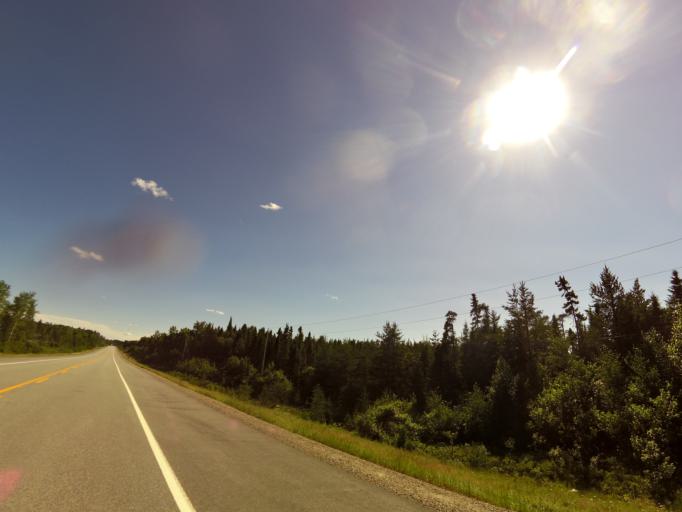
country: CA
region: Quebec
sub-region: Abitibi-Temiscamingue
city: Val-d'Or
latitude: 47.8910
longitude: -77.3437
